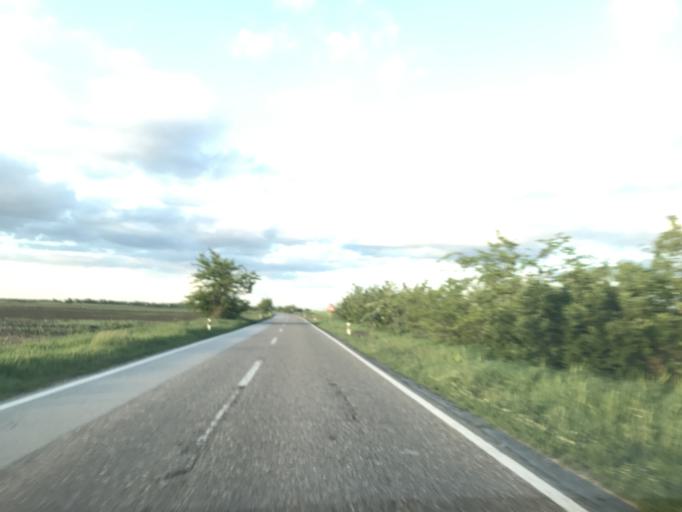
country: RS
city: Cestereg
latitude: 45.5479
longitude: 20.5123
